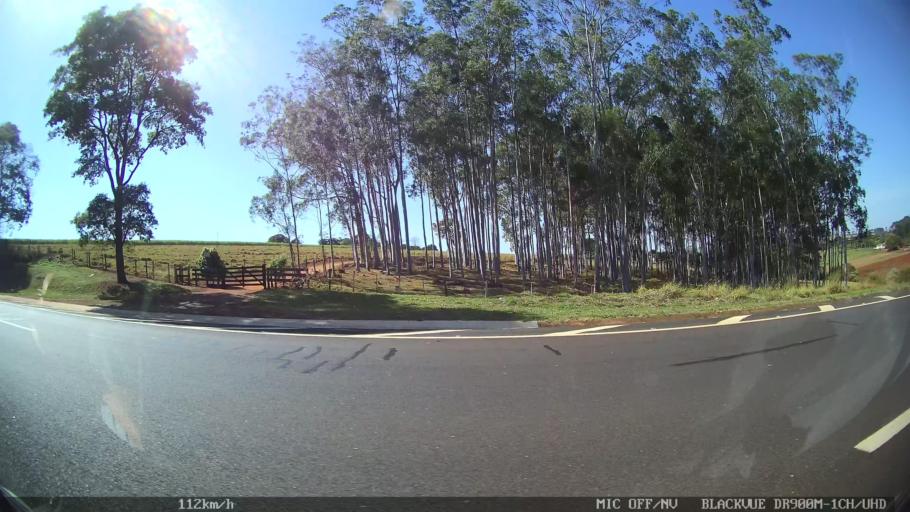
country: BR
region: Sao Paulo
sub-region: Batatais
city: Batatais
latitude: -20.8439
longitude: -47.6013
